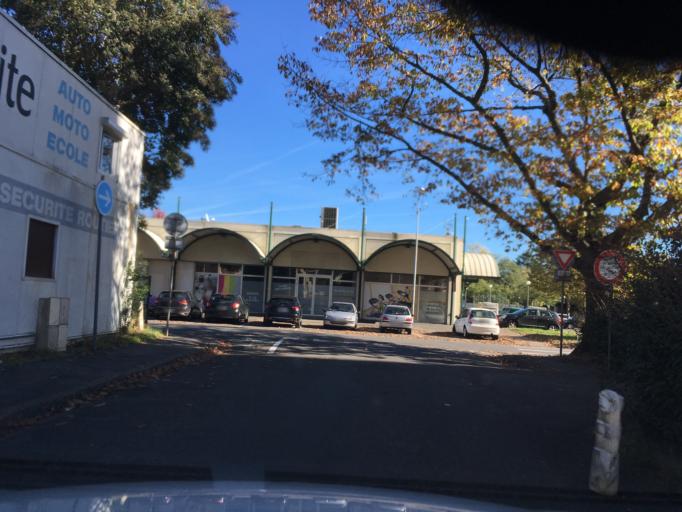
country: FR
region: Aquitaine
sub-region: Departement des Pyrenees-Atlantiques
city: Pau
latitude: 43.3110
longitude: -0.3661
